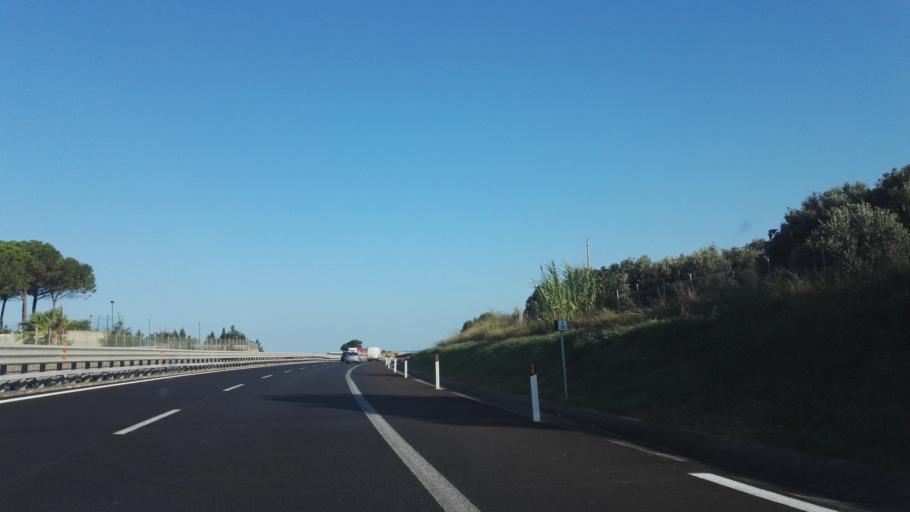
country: IT
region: Calabria
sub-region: Provincia di Catanzaro
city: Falerna Scalo
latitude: 38.9530
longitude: 16.1588
